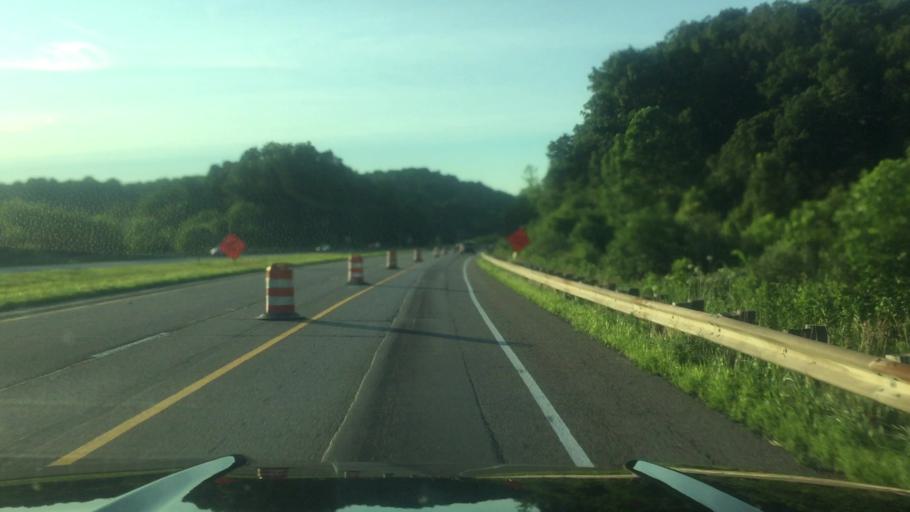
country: US
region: Ohio
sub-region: Tuscarawas County
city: Newcomerstown
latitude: 40.1760
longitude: -81.5524
